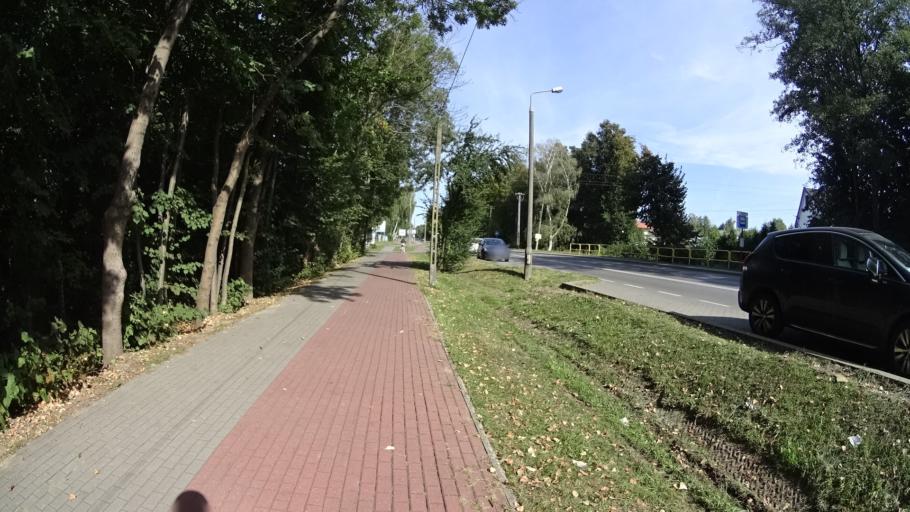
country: PL
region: Masovian Voivodeship
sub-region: Powiat legionowski
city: Nieporet
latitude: 52.4331
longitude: 21.0403
